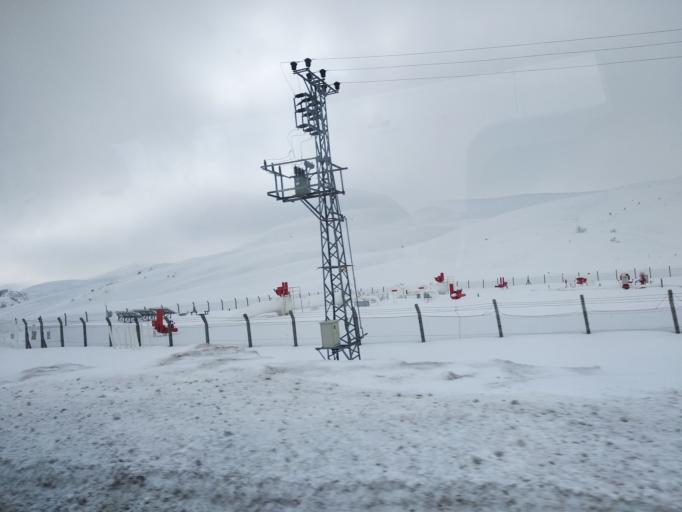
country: TR
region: Erzincan
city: Catalarmut
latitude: 39.8912
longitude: 39.3637
